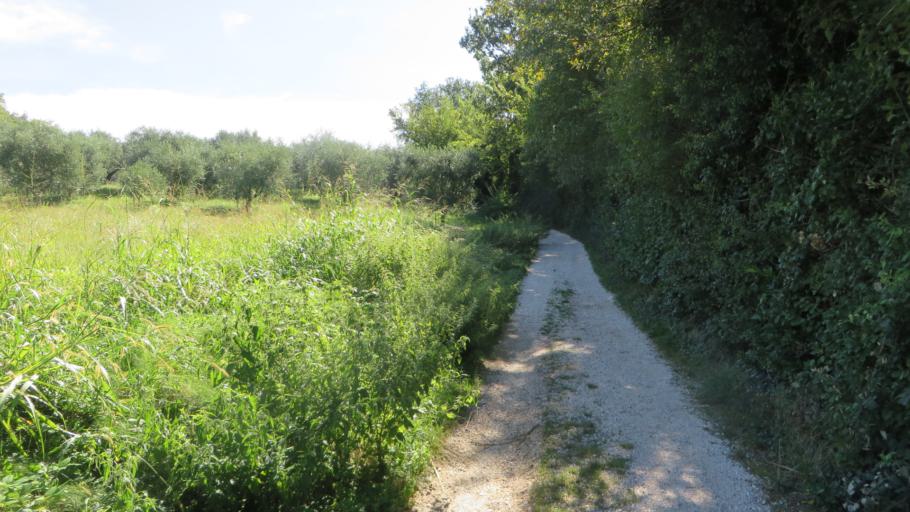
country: IT
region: Lombardy
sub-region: Provincia di Brescia
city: Solarolo
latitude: 45.5503
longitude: 10.5720
